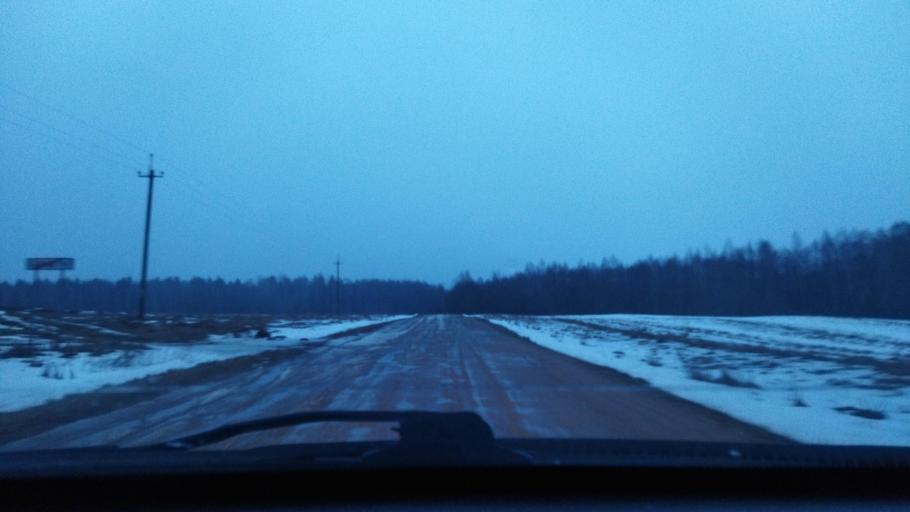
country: BY
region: Minsk
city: Svir
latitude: 54.9361
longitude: 26.3869
